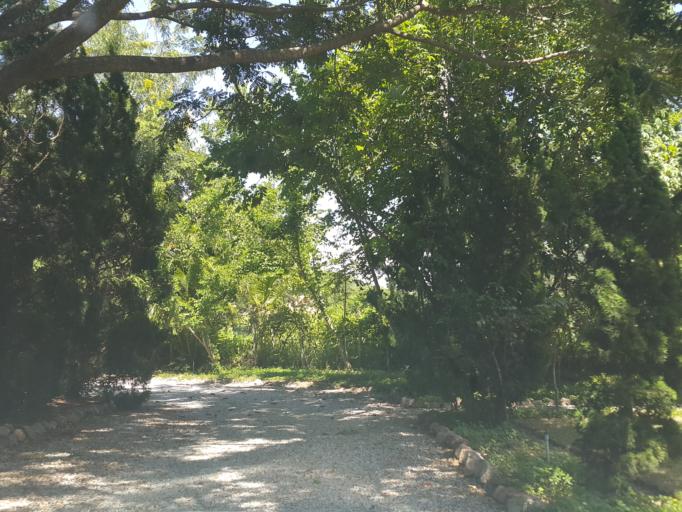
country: TH
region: Chiang Mai
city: San Kamphaeng
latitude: 18.7157
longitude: 99.1810
